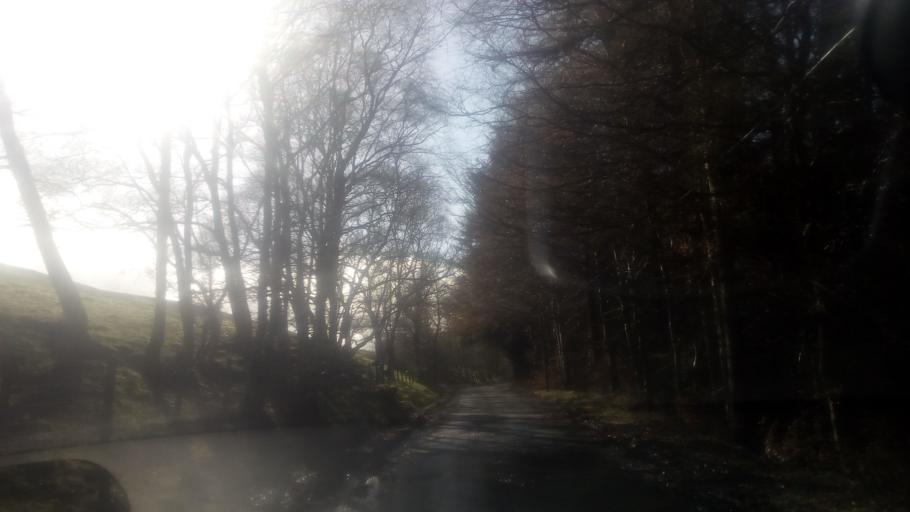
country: GB
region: Scotland
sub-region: The Scottish Borders
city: Innerleithen
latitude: 55.5107
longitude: -3.0971
